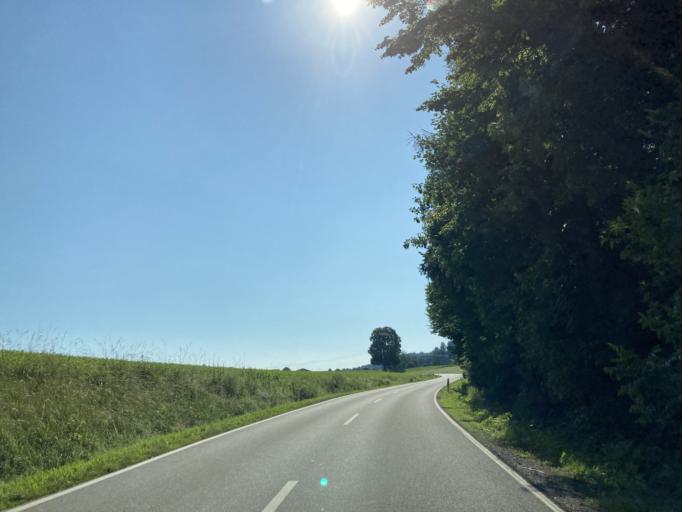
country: DE
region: Bavaria
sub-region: Upper Bavaria
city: Bad Endorf
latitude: 47.9269
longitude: 12.2919
